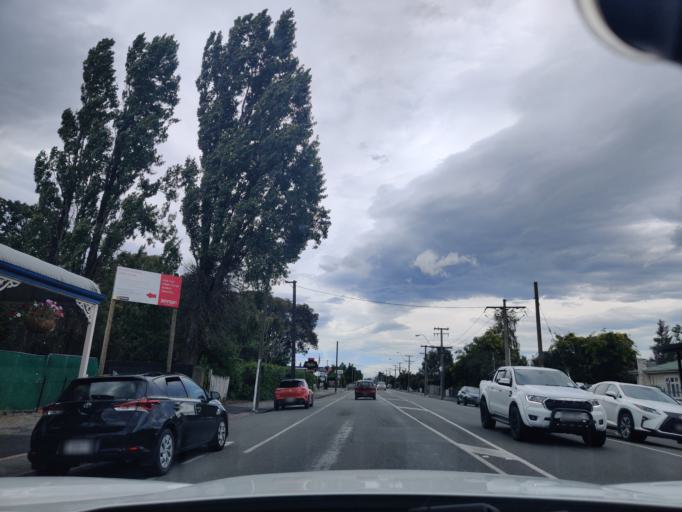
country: NZ
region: Wellington
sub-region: Masterton District
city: Masterton
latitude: -41.0226
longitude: 175.5297
